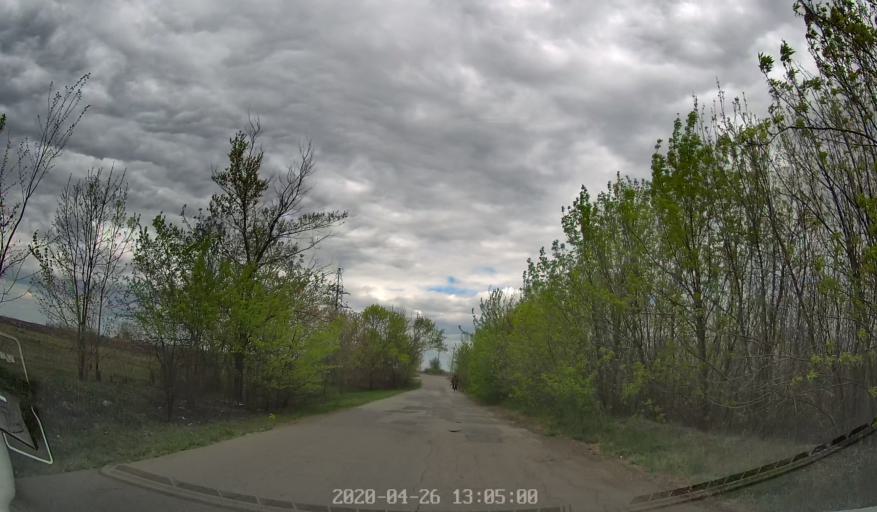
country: MD
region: Chisinau
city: Vadul lui Voda
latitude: 47.0727
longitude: 29.0664
